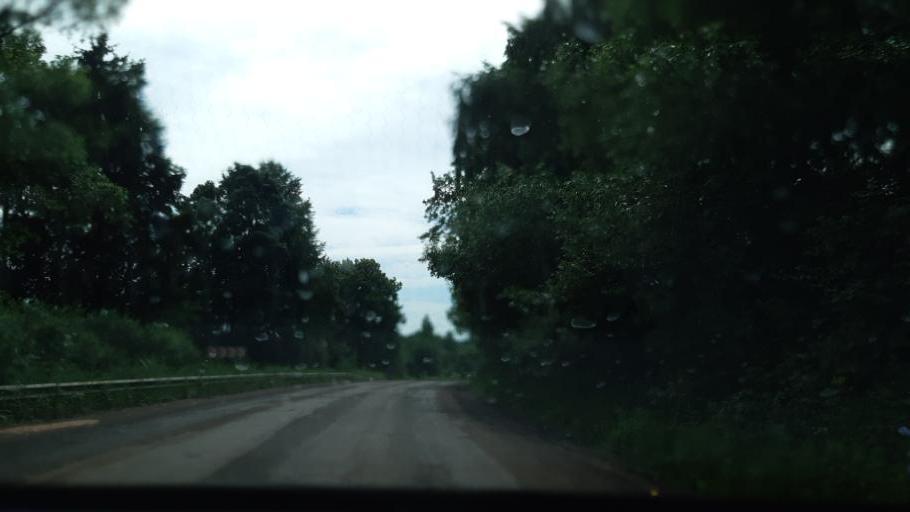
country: RU
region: Moskovskaya
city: Vereya
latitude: 55.3260
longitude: 36.1426
